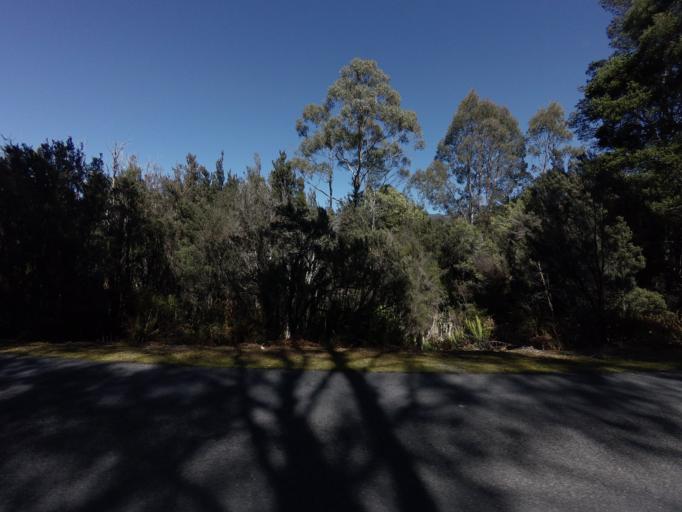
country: AU
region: Tasmania
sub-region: Derwent Valley
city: New Norfolk
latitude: -42.7549
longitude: 146.5256
